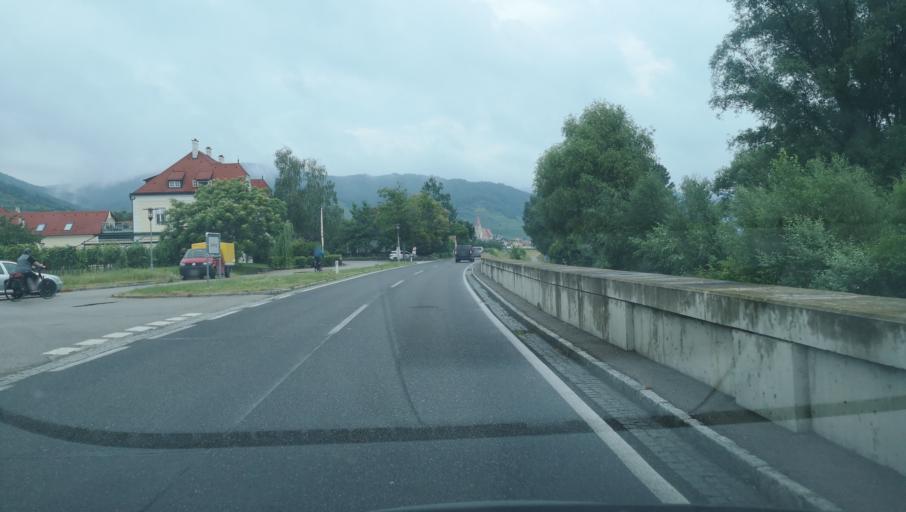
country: AT
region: Lower Austria
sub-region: Politischer Bezirk Krems
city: Weinzierl am Walde
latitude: 48.3869
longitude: 15.4620
